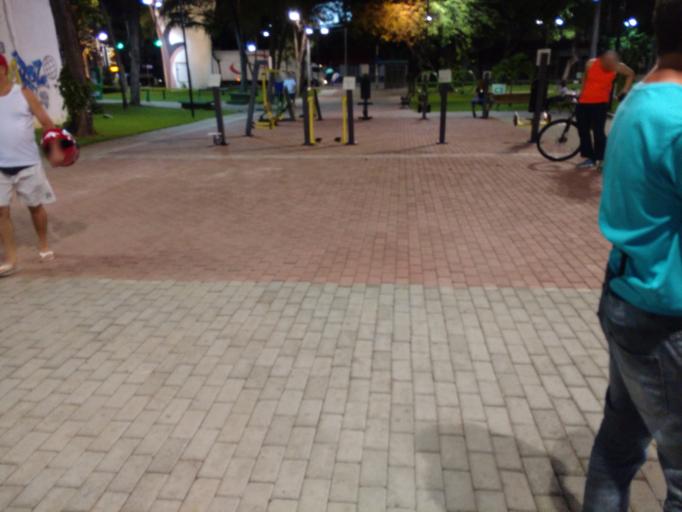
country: BR
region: Ceara
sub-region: Fortaleza
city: Fortaleza
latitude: -3.7459
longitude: -38.5021
